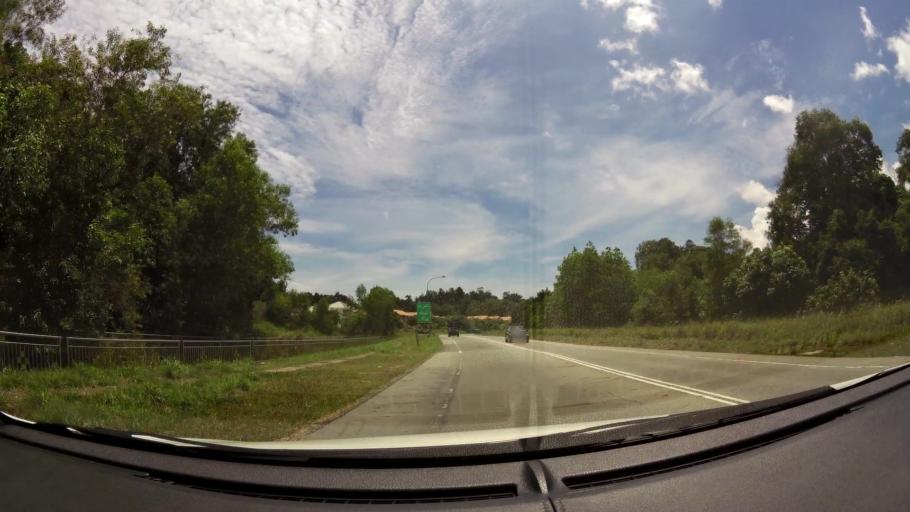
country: BN
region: Brunei and Muara
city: Bandar Seri Begawan
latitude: 4.9623
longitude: 114.9049
